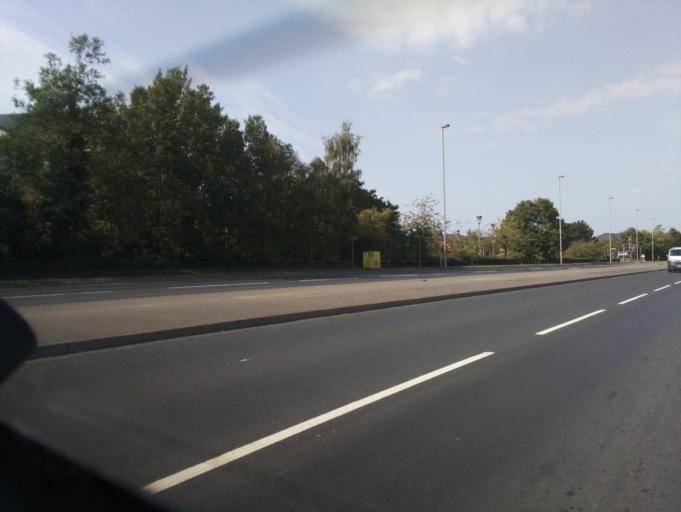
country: GB
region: England
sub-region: Staffordshire
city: Burton upon Trent
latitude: 52.7904
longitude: -1.6711
